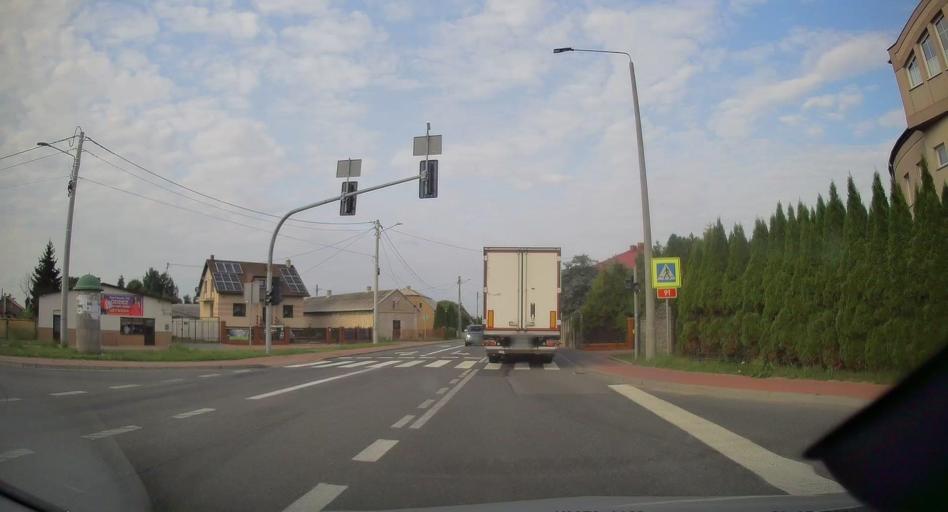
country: PL
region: Silesian Voivodeship
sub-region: Powiat czestochowski
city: Rudniki
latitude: 50.8781
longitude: 19.2461
